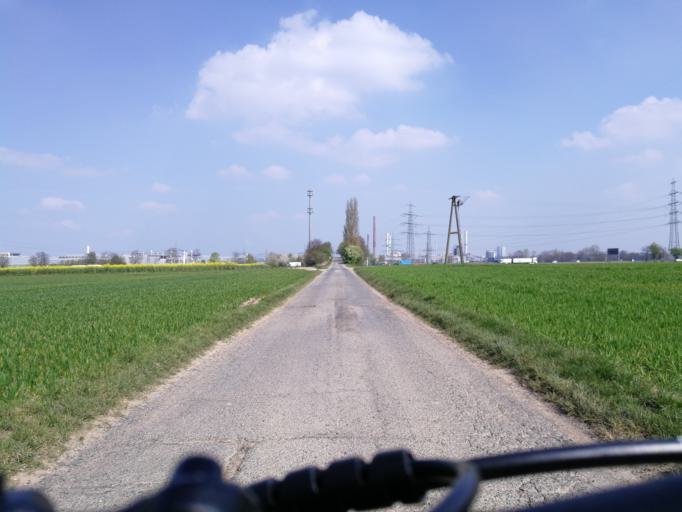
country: DE
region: North Rhine-Westphalia
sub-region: Regierungsbezirk Dusseldorf
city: Dormagen
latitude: 51.1411
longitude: 6.7655
